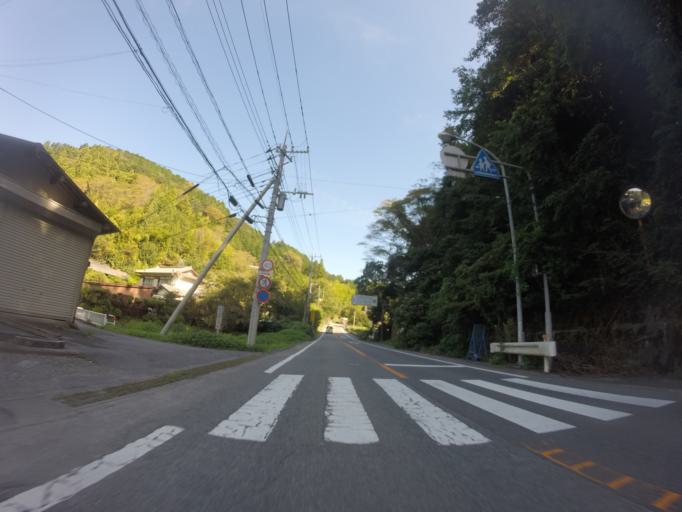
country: JP
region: Shizuoka
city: Fujinomiya
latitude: 35.3425
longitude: 138.4501
